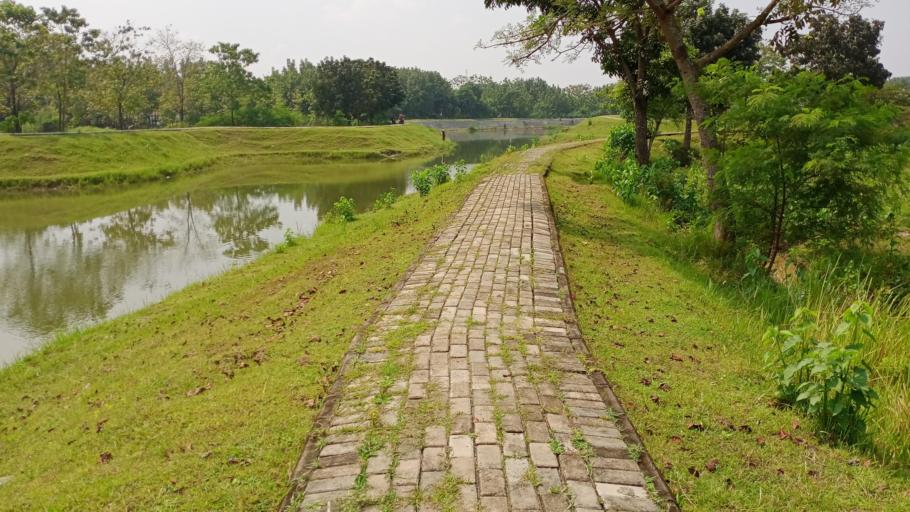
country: ID
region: West Java
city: Cileungsir
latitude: -6.3777
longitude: 107.0886
